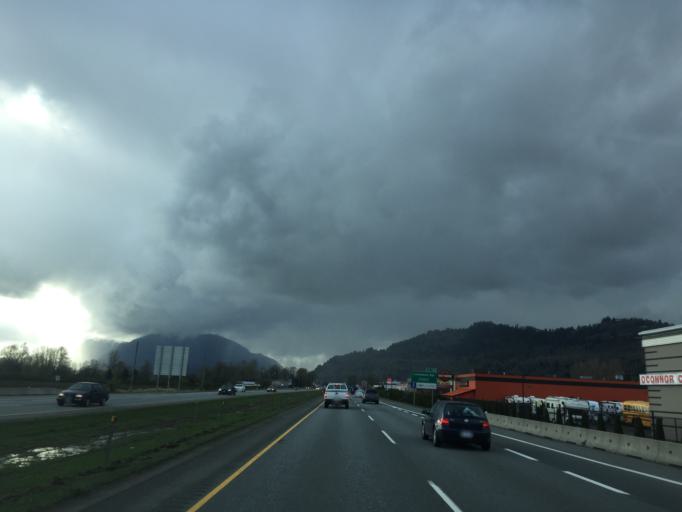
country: CA
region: British Columbia
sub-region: Fraser Valley Regional District
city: Chilliwack
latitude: 49.1440
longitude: -121.9829
